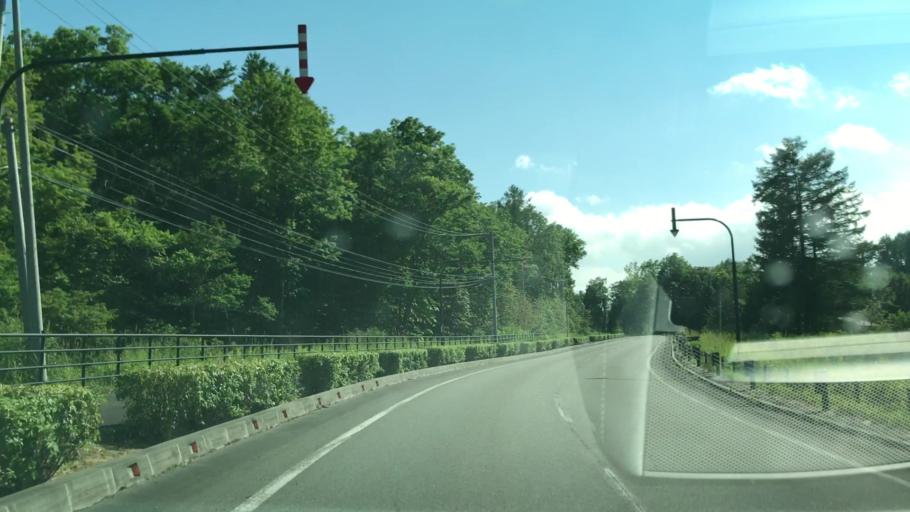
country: JP
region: Hokkaido
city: Shimo-furano
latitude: 42.8686
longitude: 142.4419
